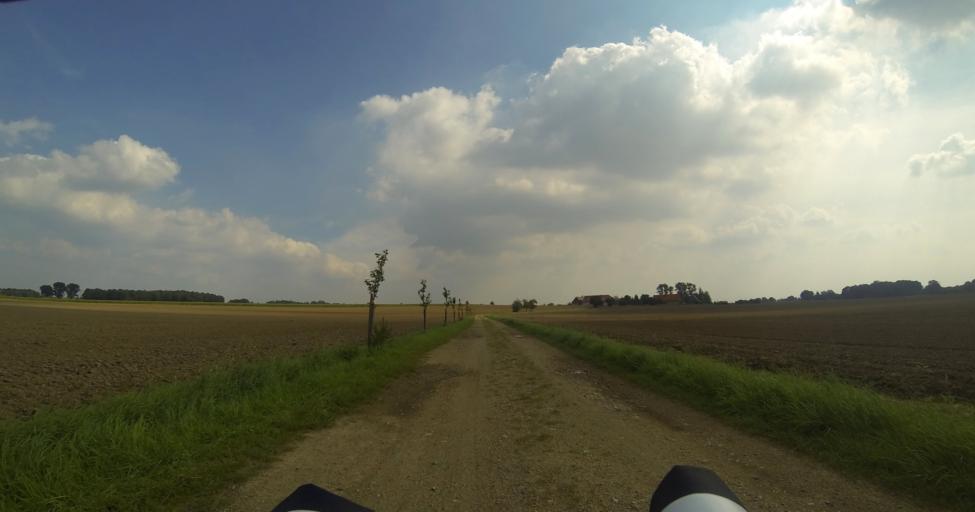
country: DE
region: Saxony
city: Grossenhain
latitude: 51.2603
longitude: 13.5587
